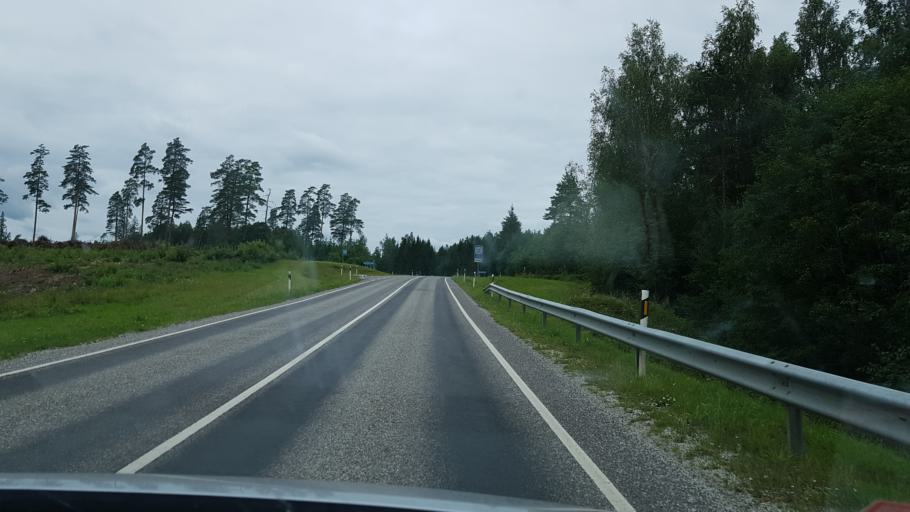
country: EE
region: Vorumaa
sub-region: Antsla vald
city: Vana-Antsla
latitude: 57.9964
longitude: 26.7255
